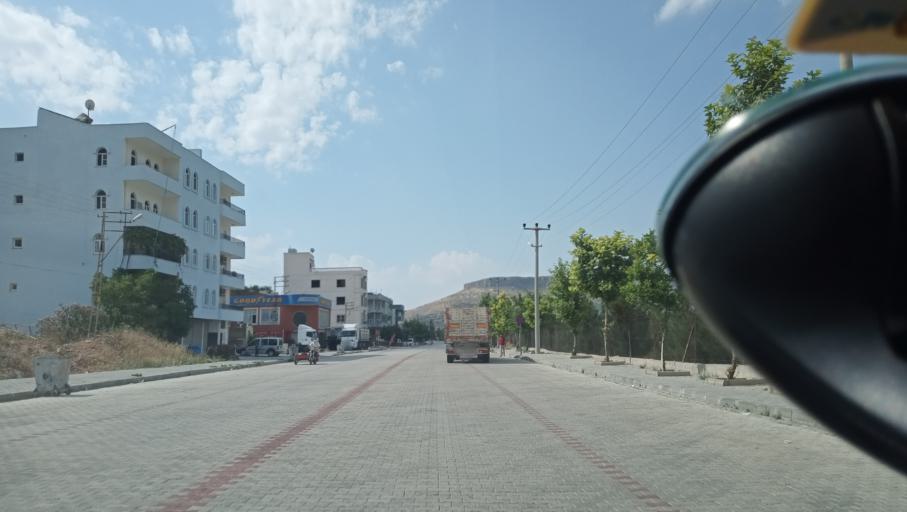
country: TR
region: Mardin
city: Kabala
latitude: 37.3462
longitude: 40.8039
